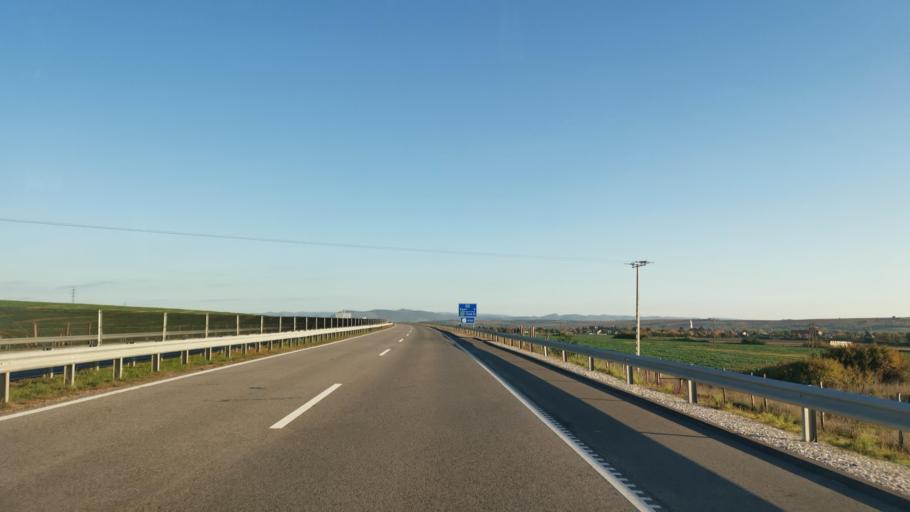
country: HU
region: Heves
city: Maklar
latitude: 47.8021
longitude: 20.3946
